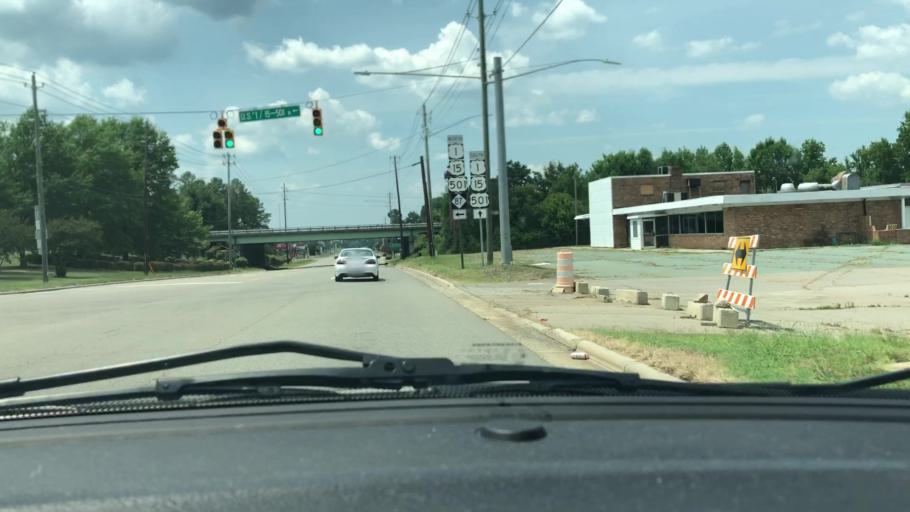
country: US
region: North Carolina
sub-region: Lee County
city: Sanford
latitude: 35.4942
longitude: -79.1938
